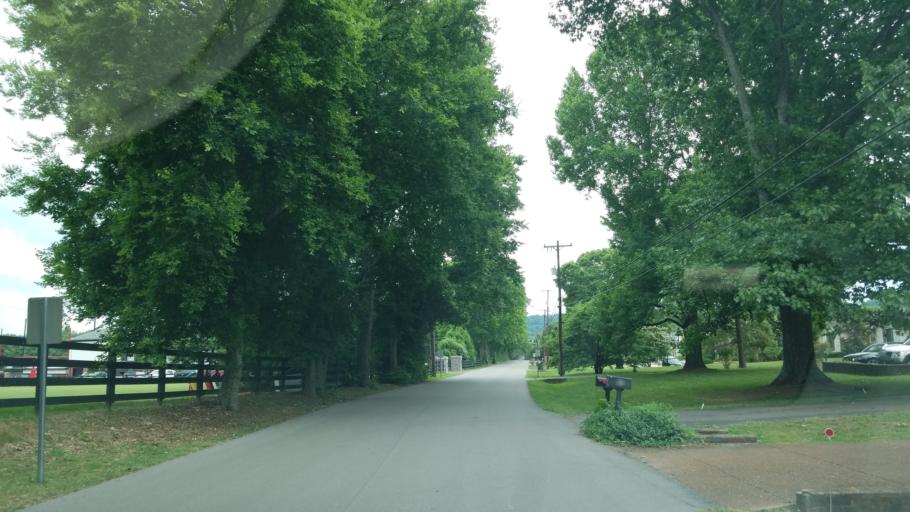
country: US
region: Tennessee
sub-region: Williamson County
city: Brentwood
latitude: 36.0339
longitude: -86.8222
